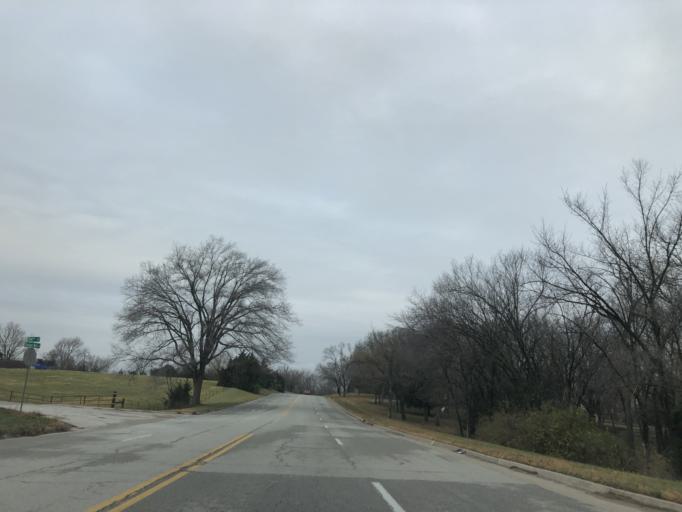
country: US
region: Kansas
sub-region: Johnson County
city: Gardner
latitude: 38.8495
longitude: -94.9319
